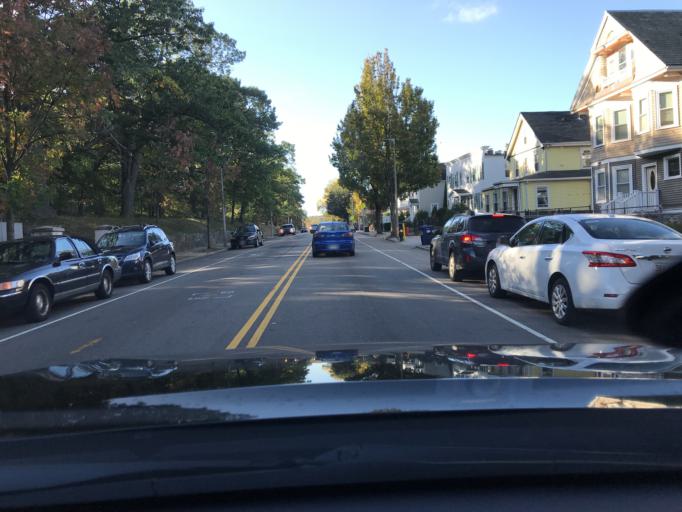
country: US
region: Massachusetts
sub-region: Norfolk County
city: Milton
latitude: 42.2767
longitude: -71.0669
